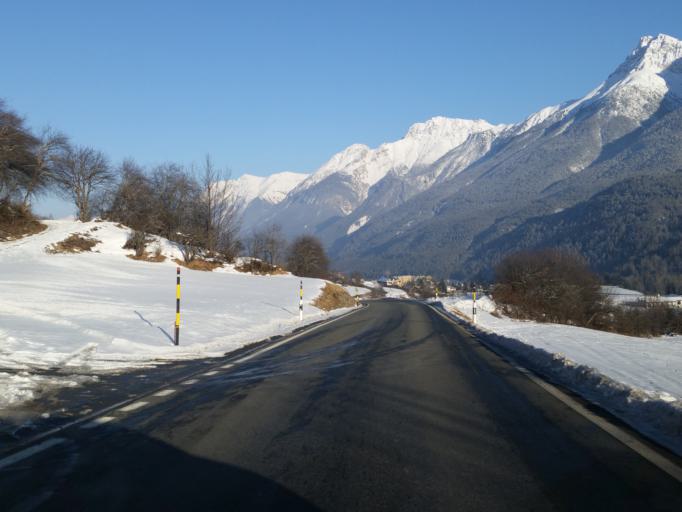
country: CH
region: Grisons
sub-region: Inn District
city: Scuol
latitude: 46.7926
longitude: 10.2769
